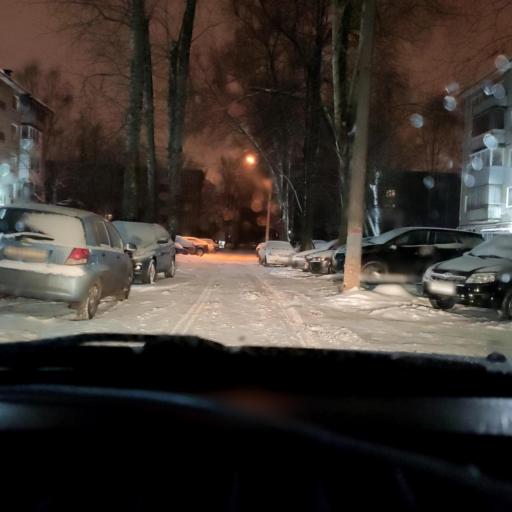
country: RU
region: Perm
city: Perm
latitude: 57.9789
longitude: 56.2926
